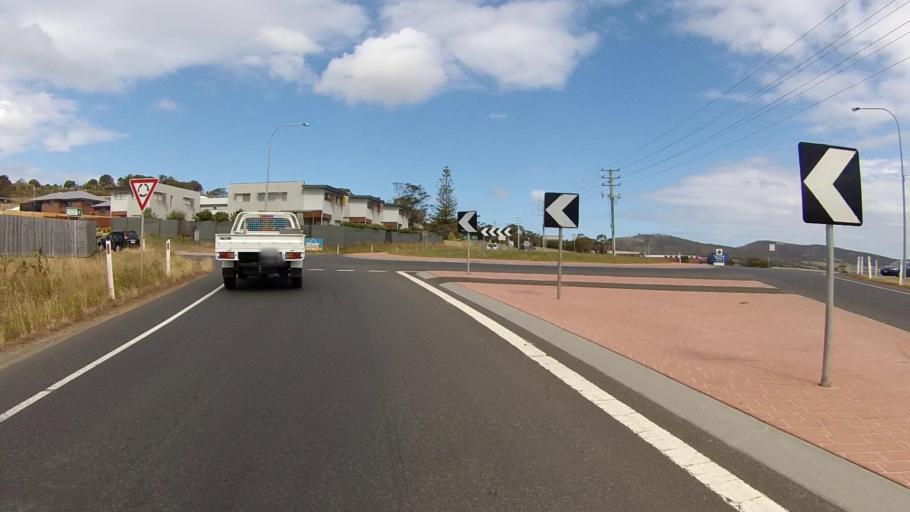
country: AU
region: Tasmania
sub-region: Clarence
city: Rokeby
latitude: -42.9058
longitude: 147.4545
